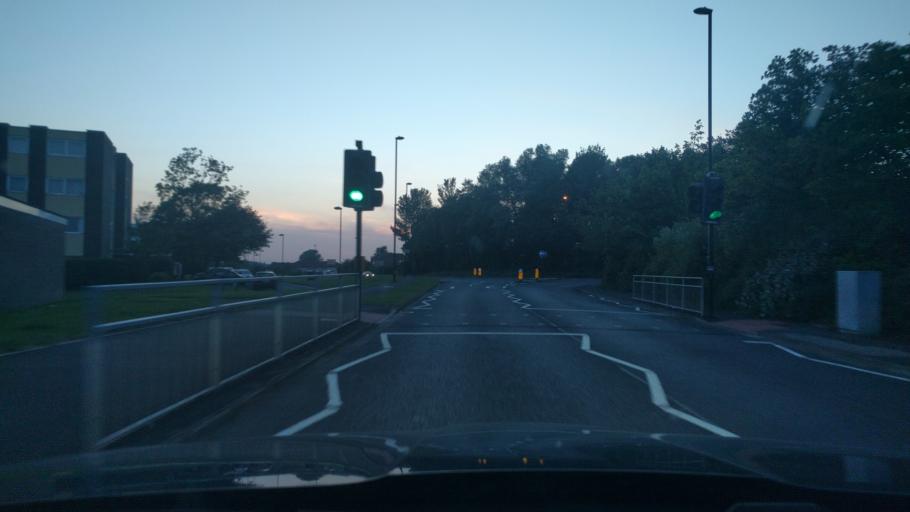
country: GB
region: England
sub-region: Northumberland
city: Seghill
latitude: 55.0347
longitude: -1.5695
